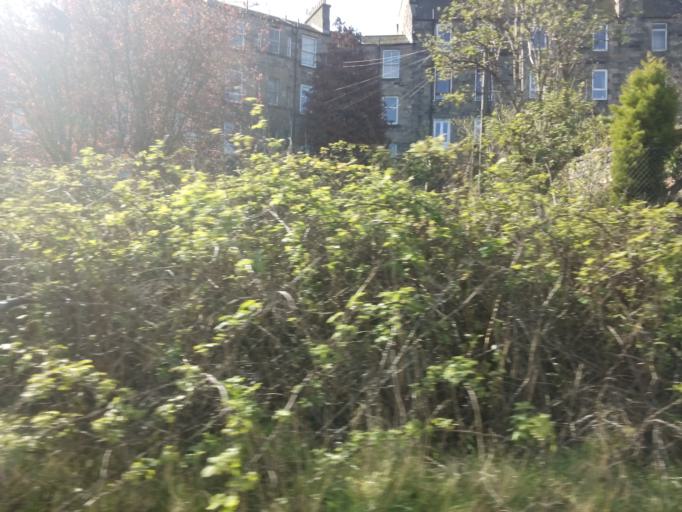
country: GB
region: Scotland
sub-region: West Lothian
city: Seafield
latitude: 55.9552
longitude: -3.1579
